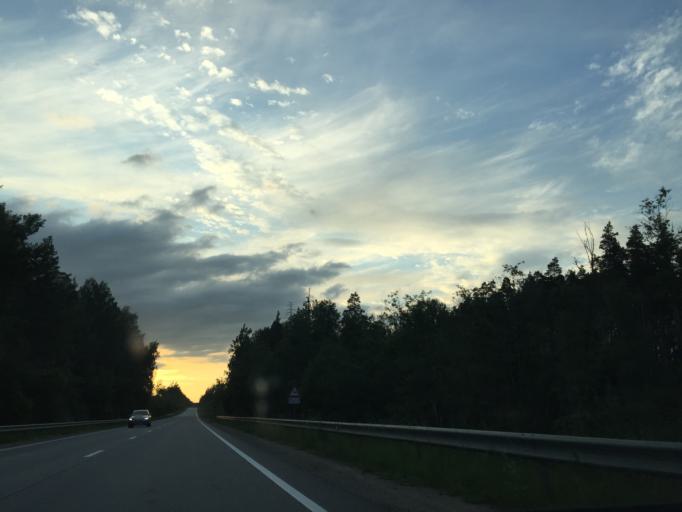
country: LV
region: Tukuma Rajons
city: Tukums
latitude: 56.9845
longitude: 23.0353
